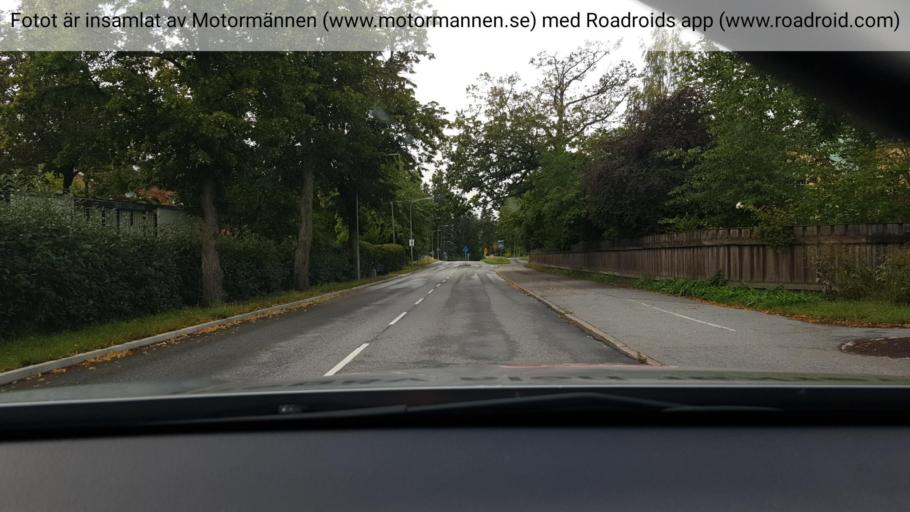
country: SE
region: Stockholm
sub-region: Danderyds Kommun
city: Djursholm
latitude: 59.3839
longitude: 18.0569
